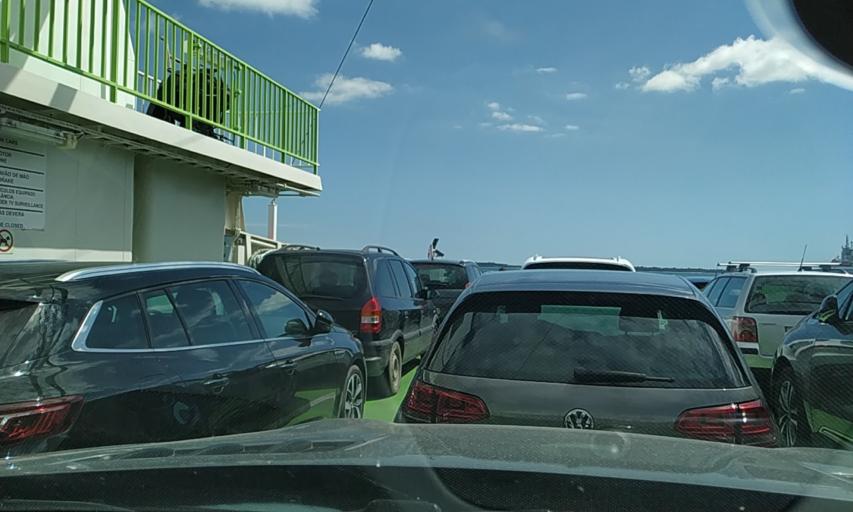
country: PT
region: Setubal
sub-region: Setubal
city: Setubal
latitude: 38.5173
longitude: -8.8858
